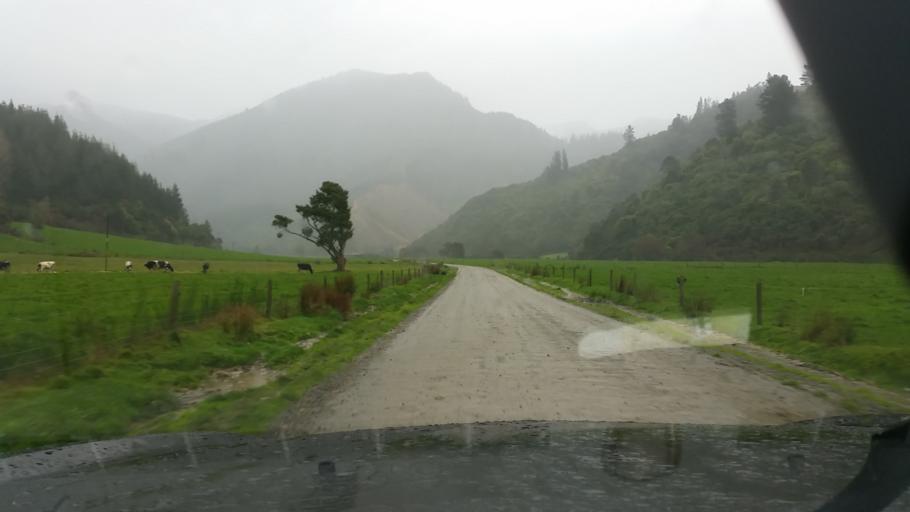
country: NZ
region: Marlborough
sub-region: Marlborough District
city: Picton
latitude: -41.3557
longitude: 173.9275
